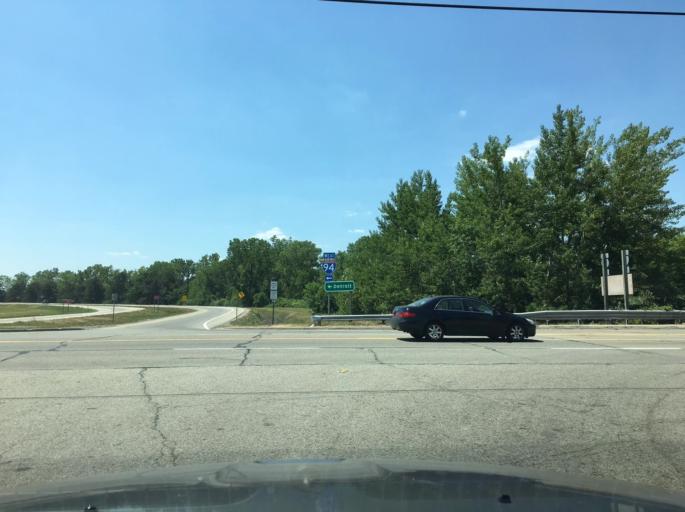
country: US
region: Michigan
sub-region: Macomb County
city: Mount Clemens
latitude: 42.5540
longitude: -82.8705
